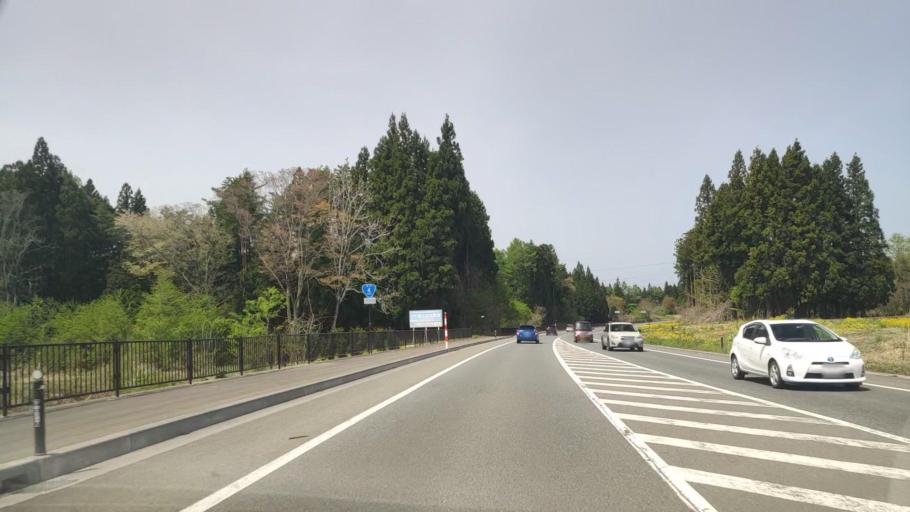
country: JP
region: Aomori
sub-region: Misawa Shi
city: Inuotose
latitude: 40.6785
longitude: 141.1724
